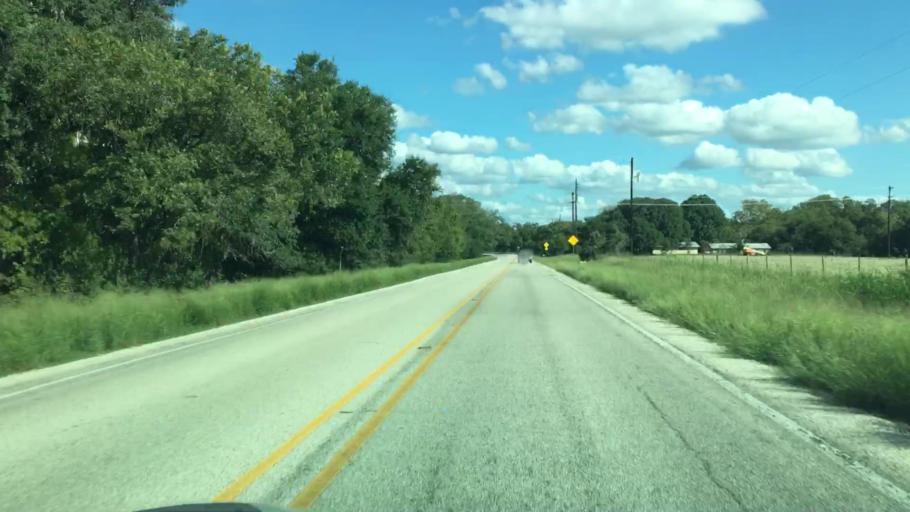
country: US
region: Texas
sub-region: Blanco County
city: Blanco
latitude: 30.0924
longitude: -98.4059
